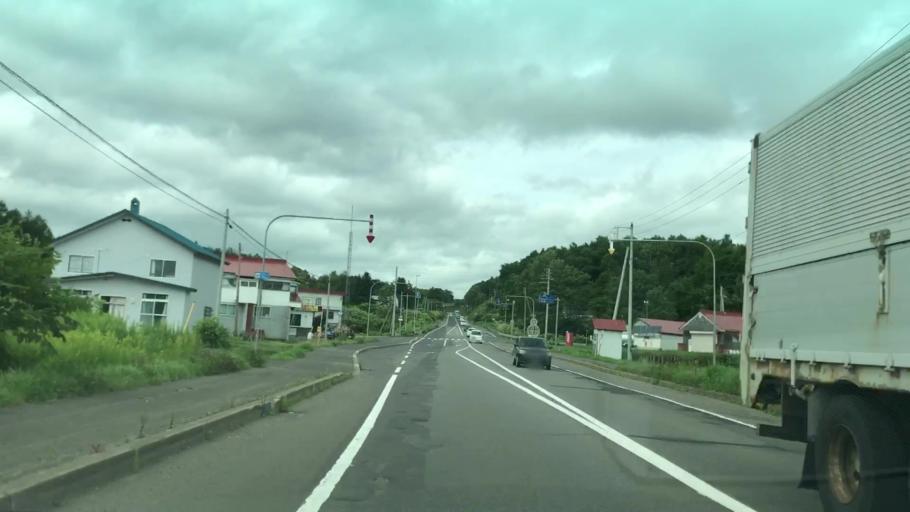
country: JP
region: Hokkaido
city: Niseko Town
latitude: 42.9215
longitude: 140.7394
